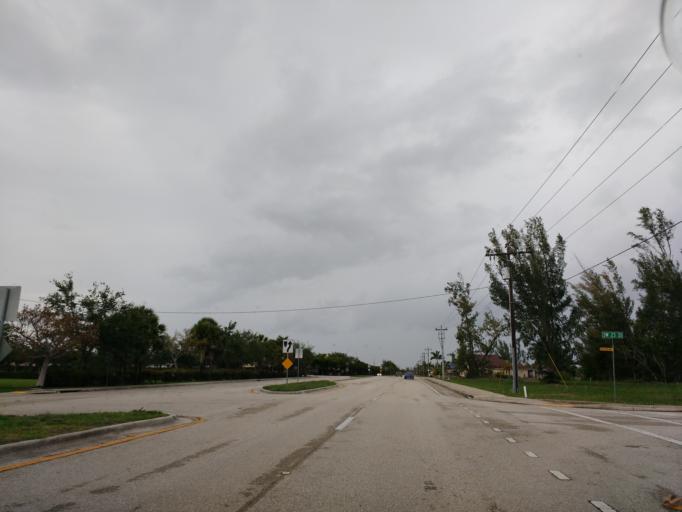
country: US
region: Florida
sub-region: Lee County
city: Cape Coral
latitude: 26.6095
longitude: -82.0233
